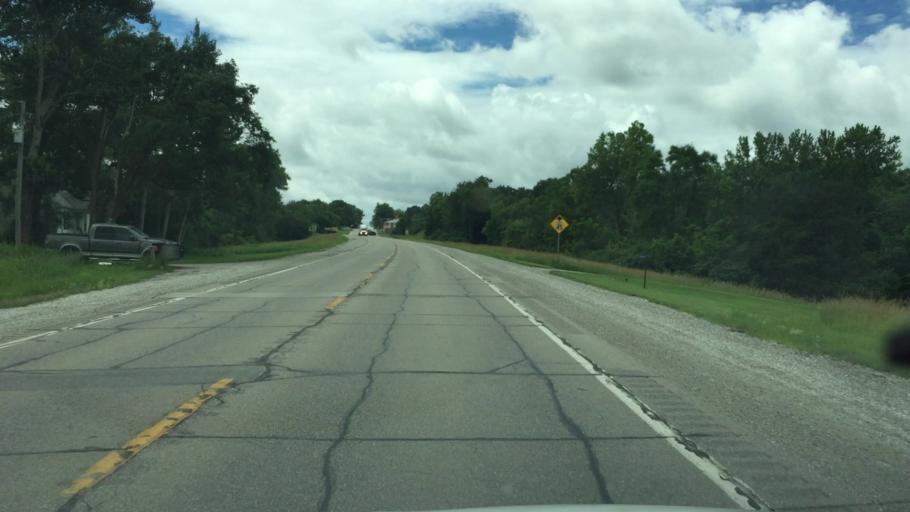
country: US
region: Iowa
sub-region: Jasper County
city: Monroe
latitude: 41.5326
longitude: -93.1019
